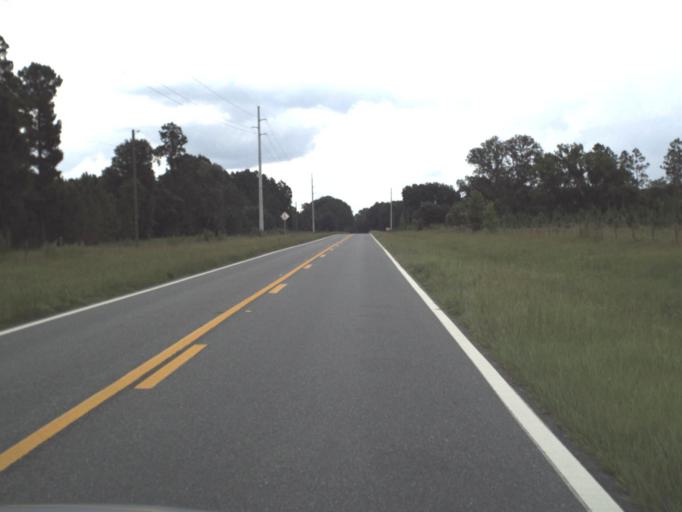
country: US
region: Florida
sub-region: Union County
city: Lake Butler
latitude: 29.9138
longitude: -82.3970
